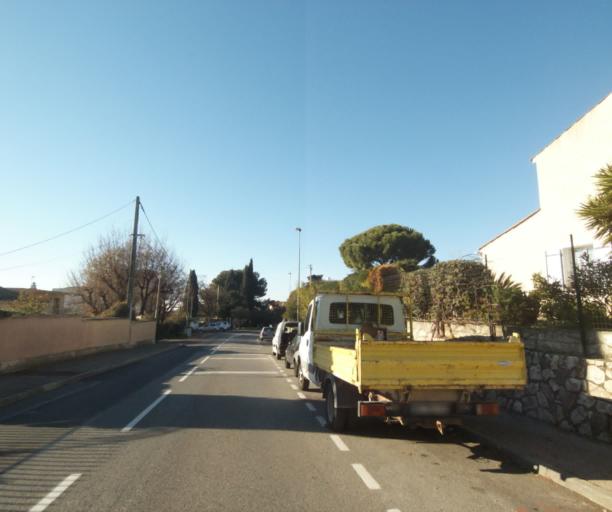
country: FR
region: Provence-Alpes-Cote d'Azur
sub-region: Departement des Alpes-Maritimes
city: Antibes
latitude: 43.5826
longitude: 7.0992
